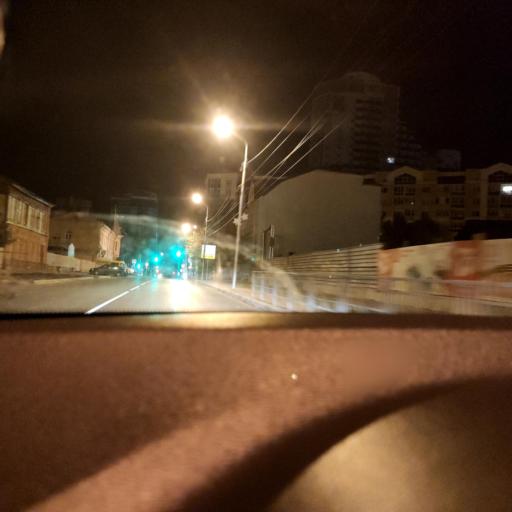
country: RU
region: Samara
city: Samara
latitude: 53.1989
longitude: 50.1093
